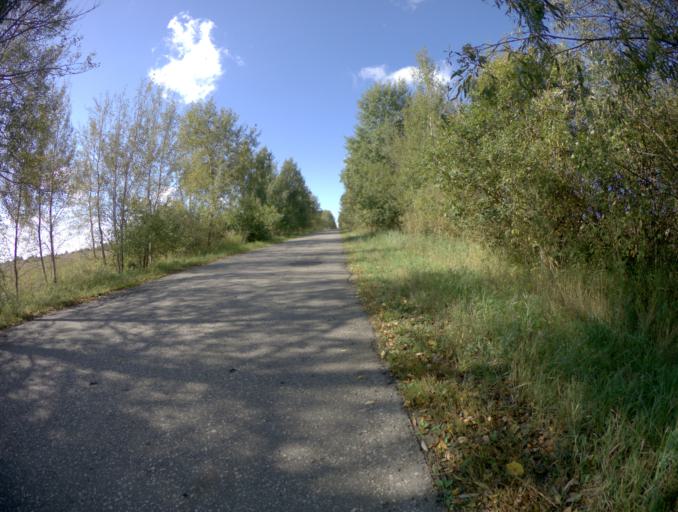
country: RU
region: Vladimir
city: Lakinsk
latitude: 55.8960
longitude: 39.8781
